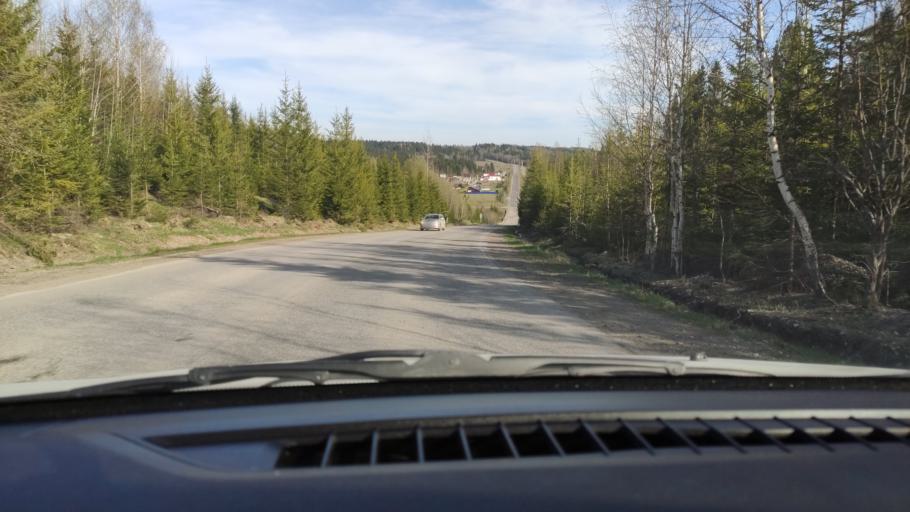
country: RU
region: Perm
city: Novyye Lyady
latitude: 57.9398
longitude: 56.6224
